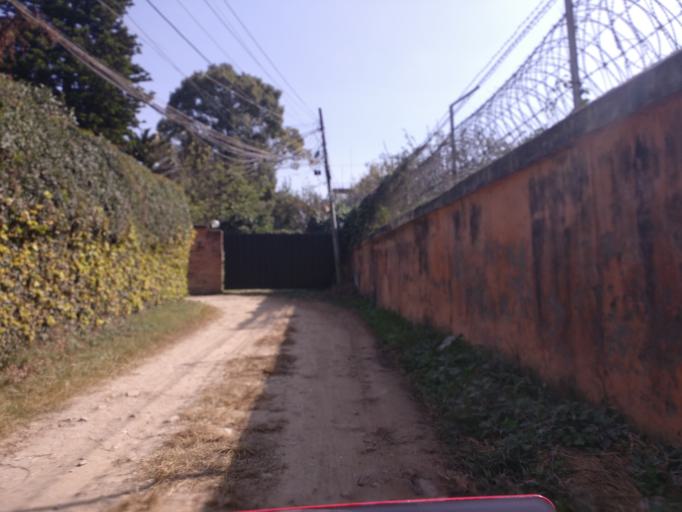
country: NP
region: Central Region
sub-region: Bagmati Zone
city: Patan
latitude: 27.6695
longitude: 85.3150
